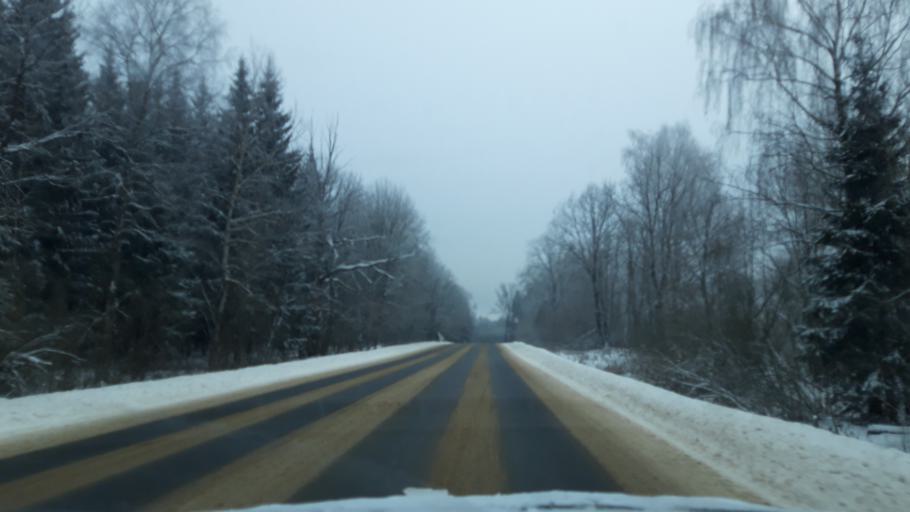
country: RU
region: Moskovskaya
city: Avtopoligon
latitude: 56.2778
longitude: 37.3710
